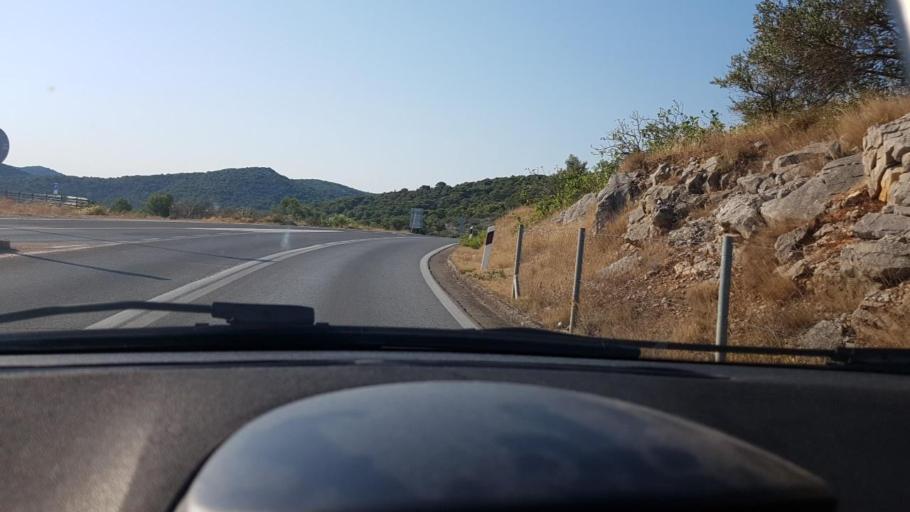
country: HR
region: Sibensko-Kniniska
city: Murter
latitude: 43.8118
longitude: 15.6018
